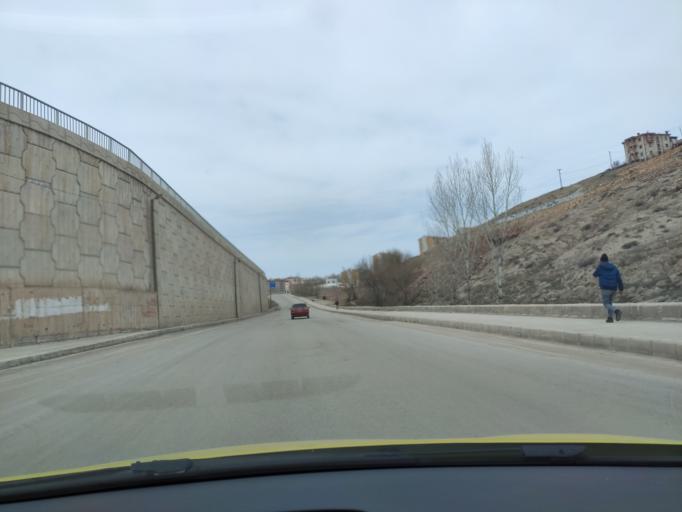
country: TR
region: Bayburt
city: Bayburt
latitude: 40.2567
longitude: 40.2187
